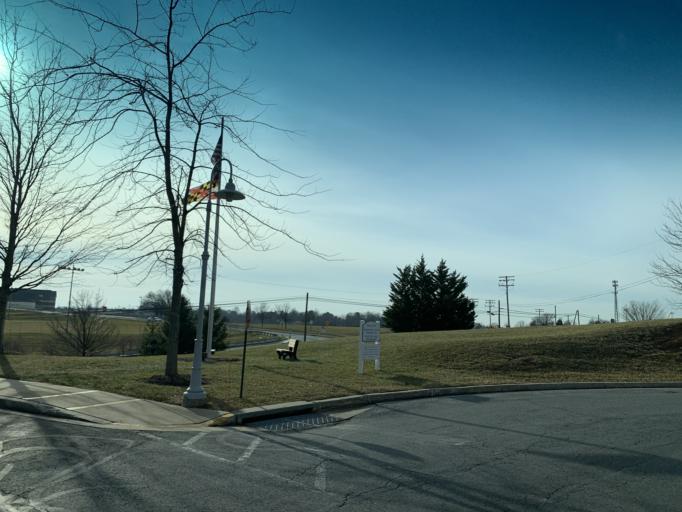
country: US
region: Maryland
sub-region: Carroll County
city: Westminster
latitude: 39.5705
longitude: -76.9734
